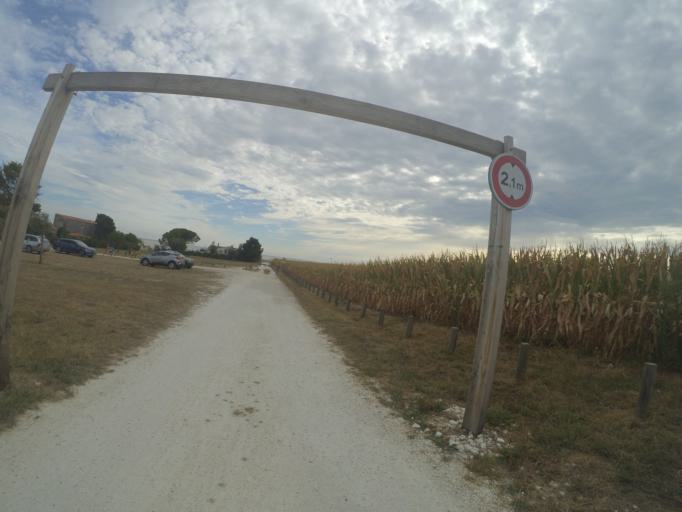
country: FR
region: Poitou-Charentes
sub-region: Departement de la Charente-Maritime
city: Meschers-sur-Gironde
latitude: 45.5524
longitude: -0.9204
